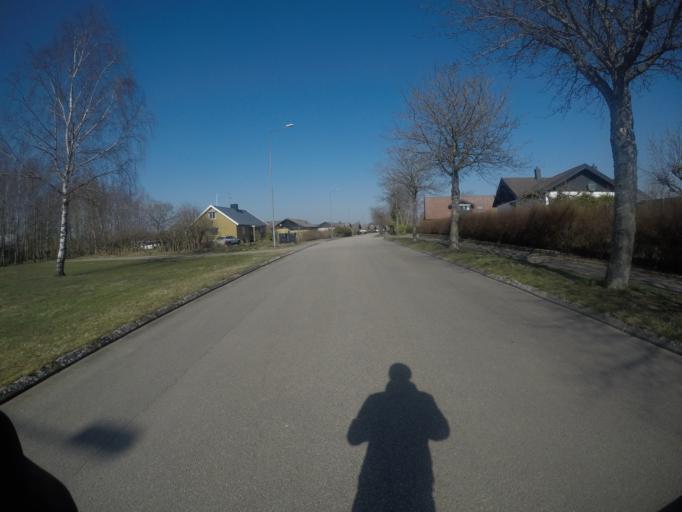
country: SE
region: Halland
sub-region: Laholms Kommun
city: Laholm
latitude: 56.5003
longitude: 13.0456
